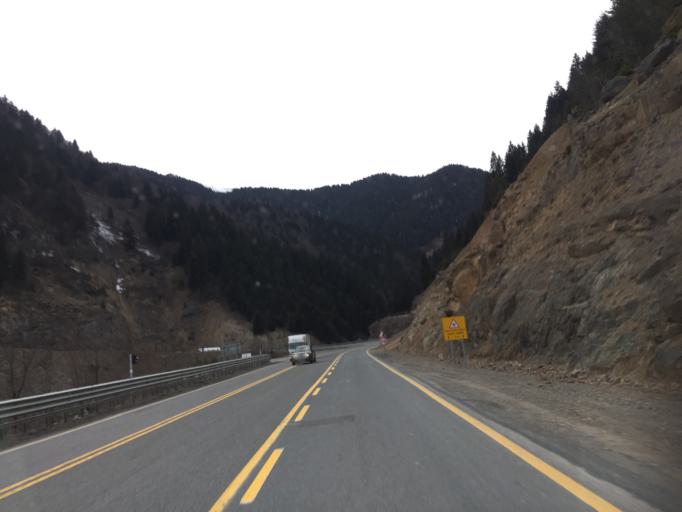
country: TR
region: Gumushane
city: Yaglidere
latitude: 40.6992
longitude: 39.4694
